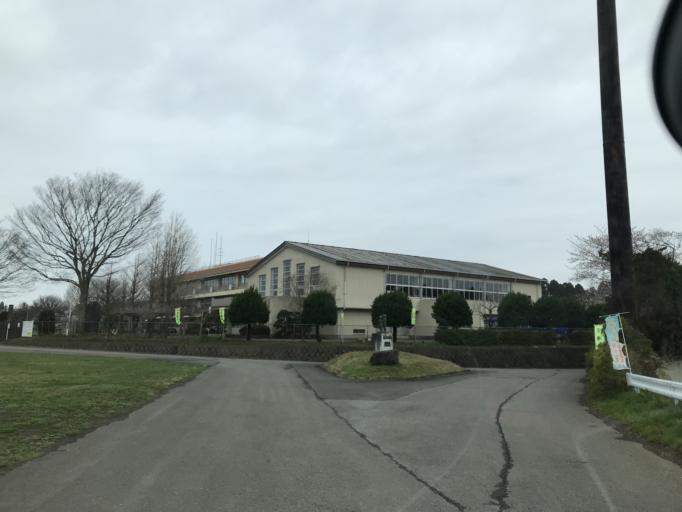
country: JP
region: Chiba
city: Sawara
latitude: 35.8113
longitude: 140.5086
